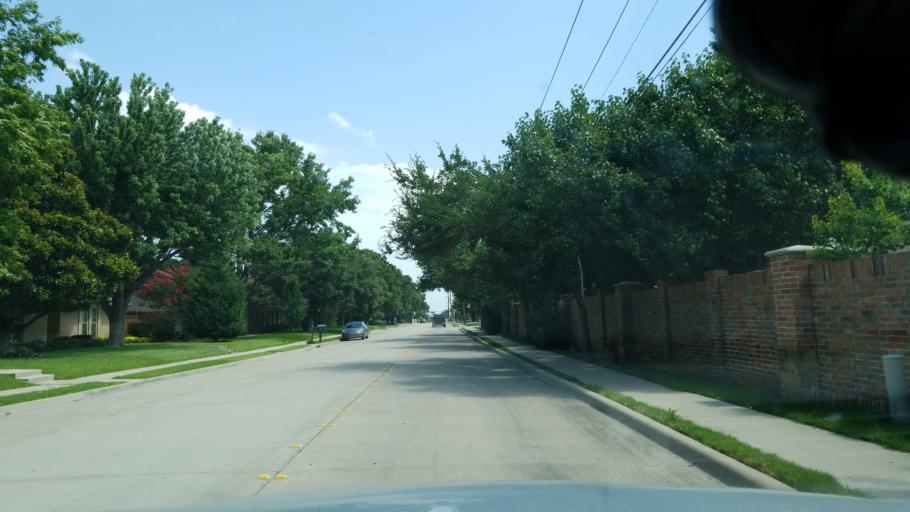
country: US
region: Texas
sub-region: Dallas County
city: Coppell
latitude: 32.9661
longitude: -96.9891
